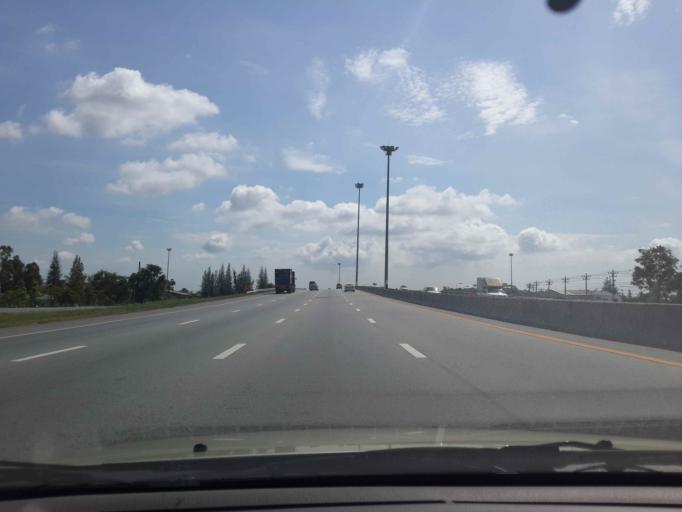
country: TH
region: Chon Buri
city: Chon Buri
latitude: 13.3434
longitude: 101.0270
